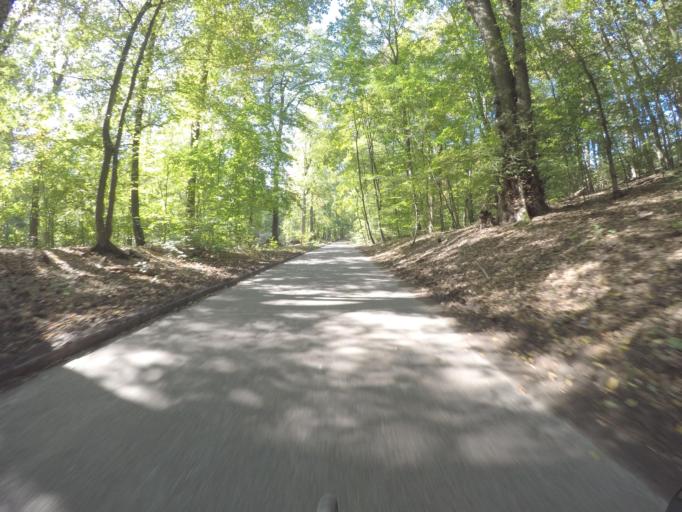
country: DE
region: Berlin
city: Heiligensee
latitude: 52.5922
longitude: 13.2597
